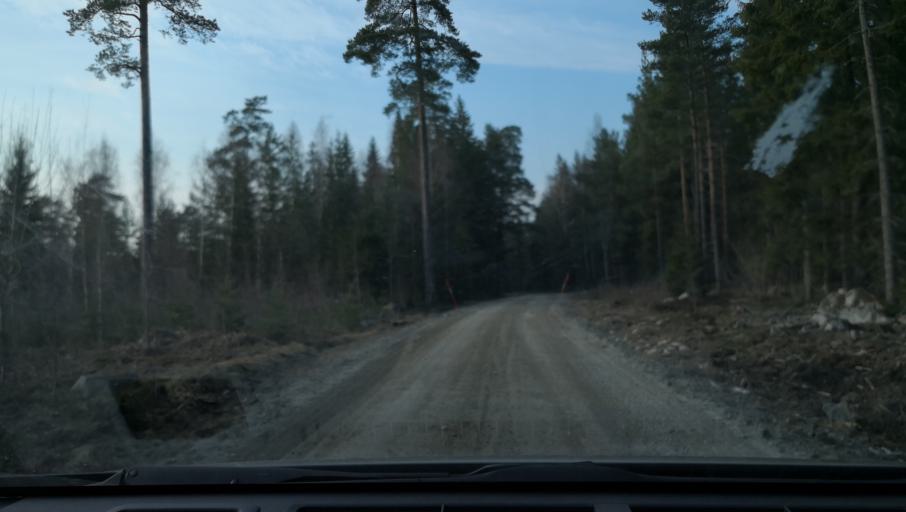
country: SE
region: OErebro
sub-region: Orebro Kommun
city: Hovsta
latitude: 59.3724
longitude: 15.3182
